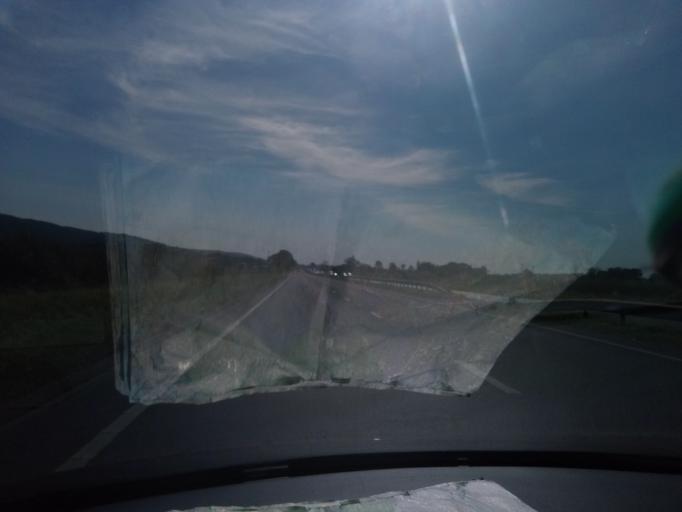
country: GB
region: England
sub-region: Stockton-on-Tees
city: Yarm
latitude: 54.4107
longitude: -1.3190
